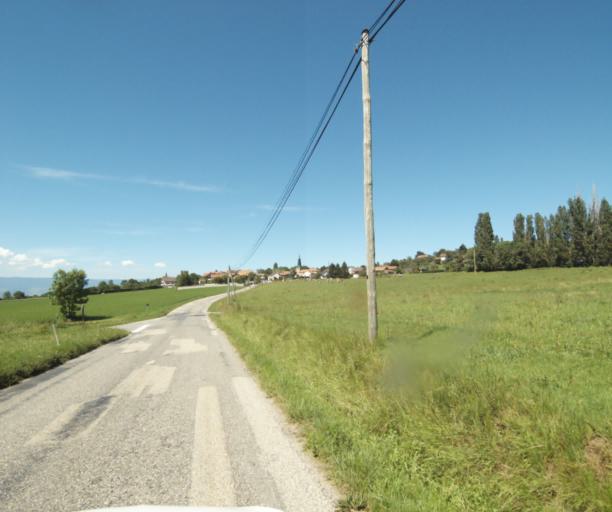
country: FR
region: Rhone-Alpes
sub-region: Departement de la Haute-Savoie
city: Ballaison
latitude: 46.2953
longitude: 6.3268
